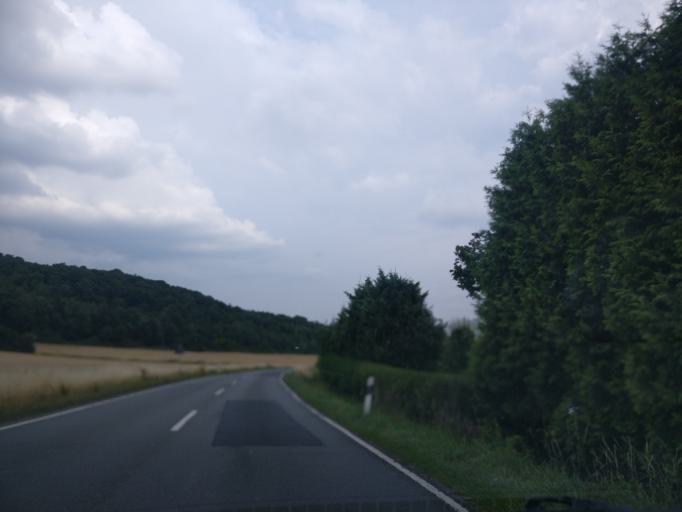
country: DE
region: Lower Saxony
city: Adelebsen
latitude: 51.5927
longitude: 9.7878
